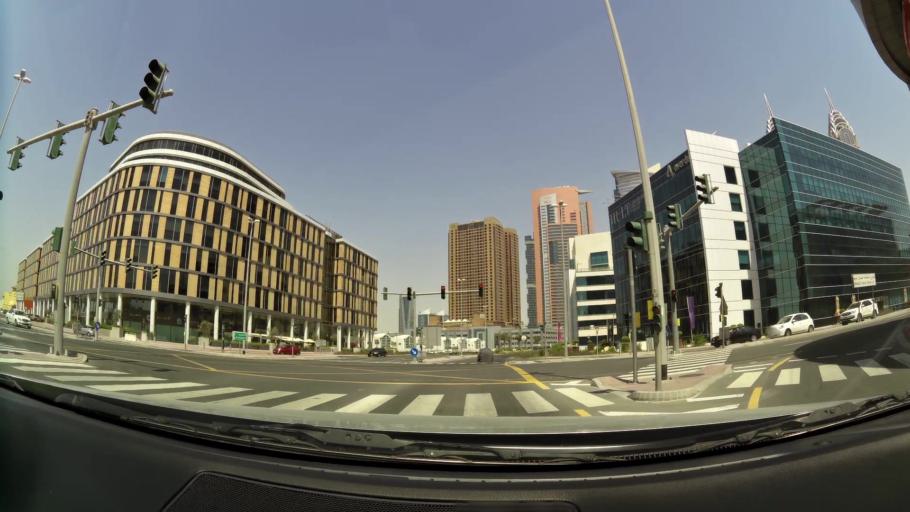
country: AE
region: Dubai
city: Dubai
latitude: 25.1046
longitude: 55.1672
